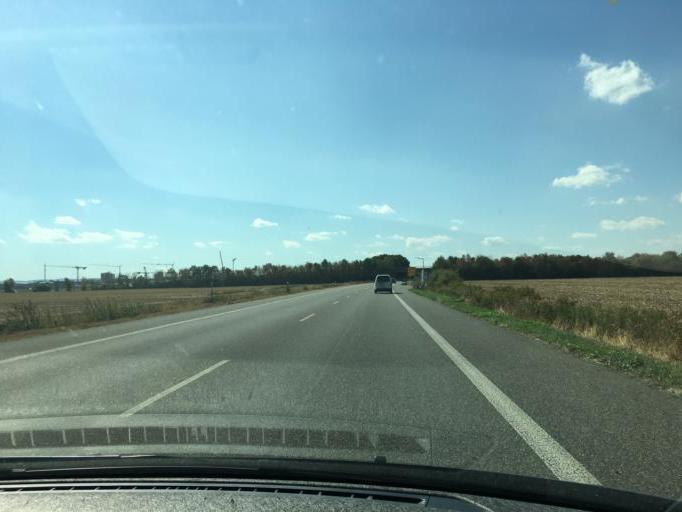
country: DE
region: North Rhine-Westphalia
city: Zulpich
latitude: 50.7082
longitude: 6.6722
